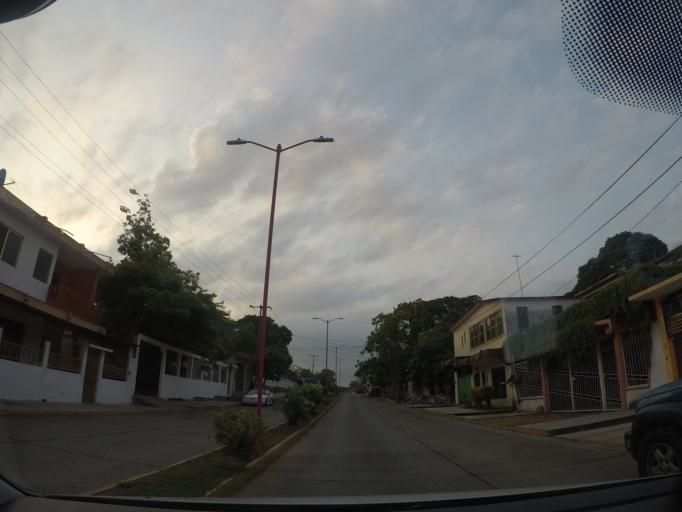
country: MX
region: Oaxaca
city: Matias Romero
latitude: 16.8754
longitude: -95.0378
